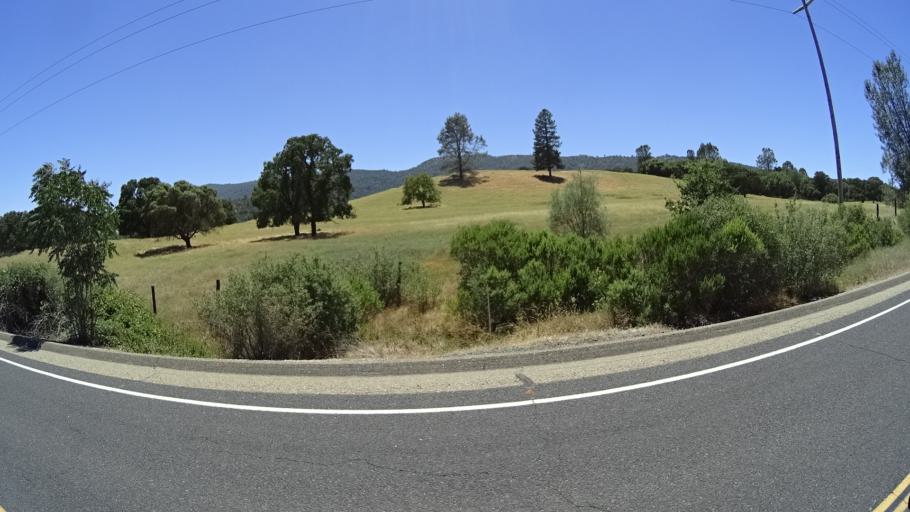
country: US
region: California
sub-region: Calaveras County
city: San Andreas
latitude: 38.1871
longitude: -120.6874
